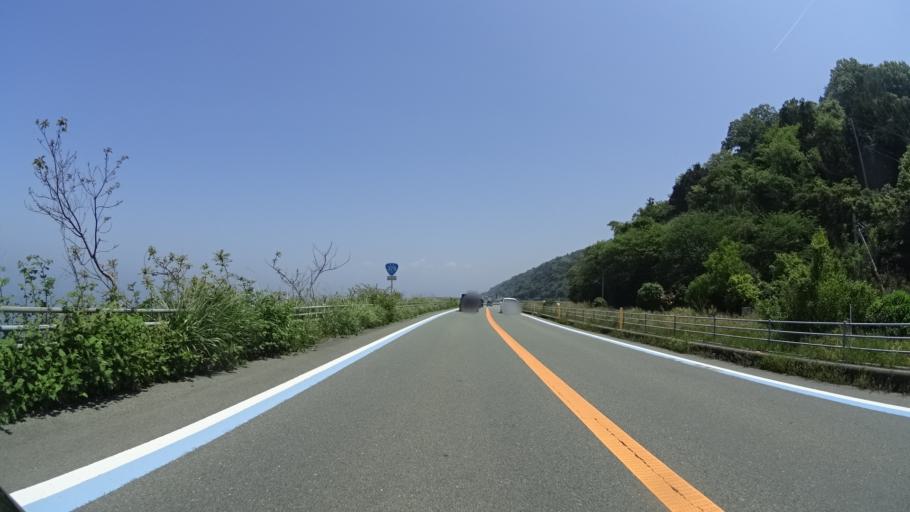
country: JP
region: Ehime
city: Ozu
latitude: 33.6280
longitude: 132.5123
